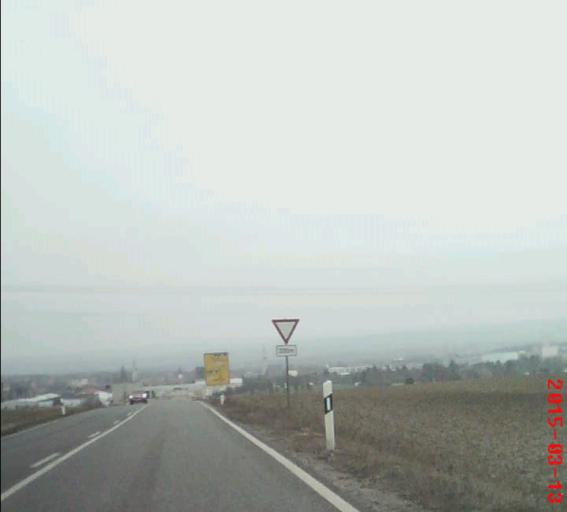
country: DE
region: Thuringia
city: Bad Langensalza
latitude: 51.0896
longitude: 10.6424
